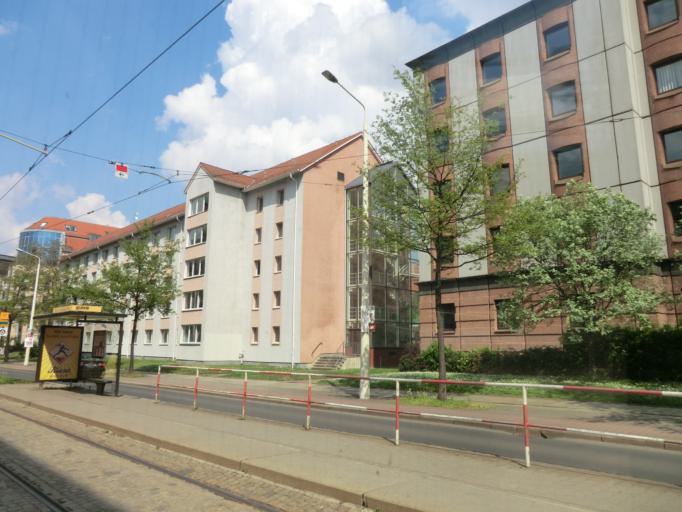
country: DE
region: Saxony
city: Dresden
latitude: 51.0596
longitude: 13.7528
